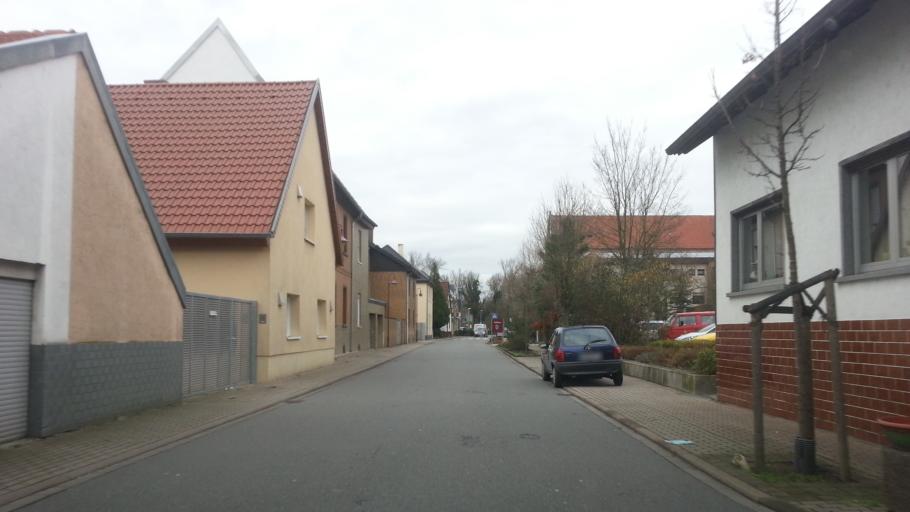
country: DE
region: Baden-Wuerttemberg
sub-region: Karlsruhe Region
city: Ketsch
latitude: 49.3665
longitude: 8.5245
